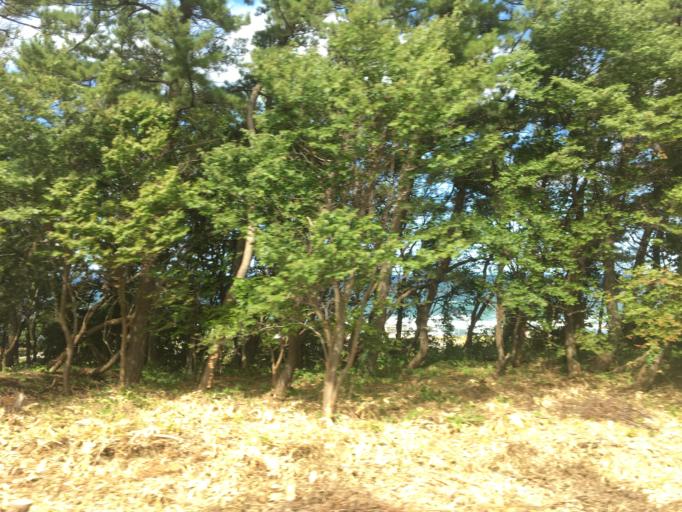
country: JP
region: Aomori
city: Shimokizukuri
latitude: 40.7716
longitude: 140.1773
